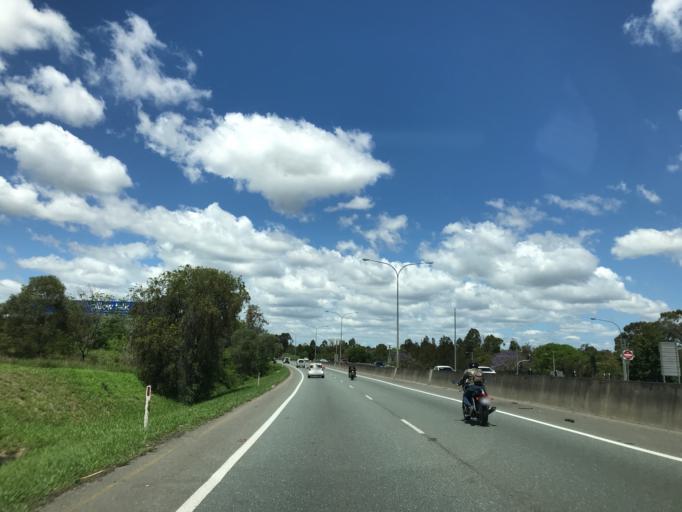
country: AU
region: Queensland
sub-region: Brisbane
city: Seventeen Mile Rocks
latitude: -27.5312
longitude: 152.9465
